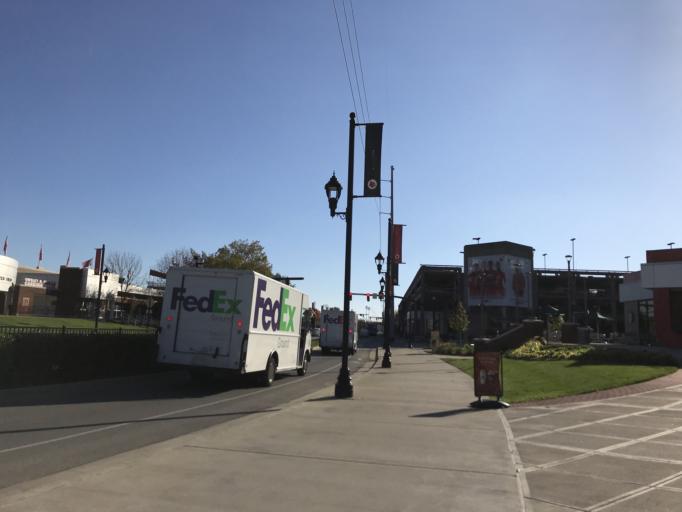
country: US
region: Kentucky
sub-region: Jefferson County
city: Audubon Park
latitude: 38.2177
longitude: -85.7547
